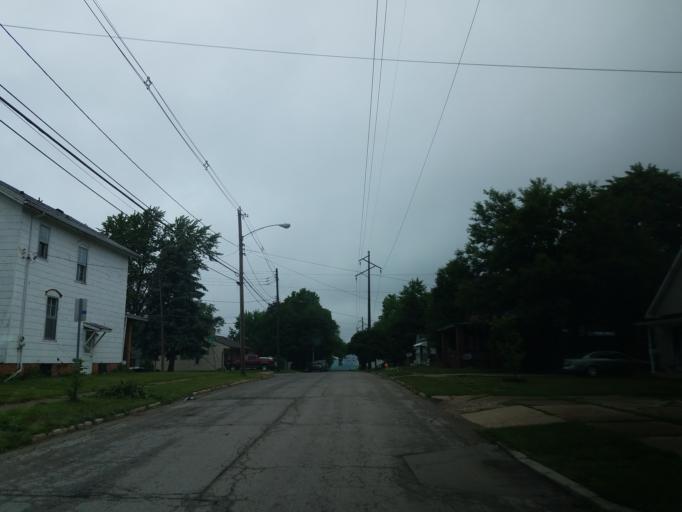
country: US
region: Illinois
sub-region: McLean County
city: Bloomington
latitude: 40.4720
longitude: -88.9819
